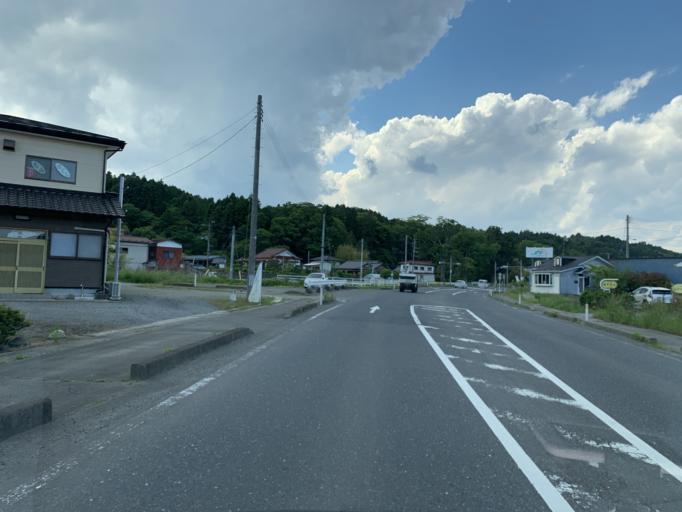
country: JP
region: Miyagi
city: Wakuya
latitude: 38.5451
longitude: 141.1420
